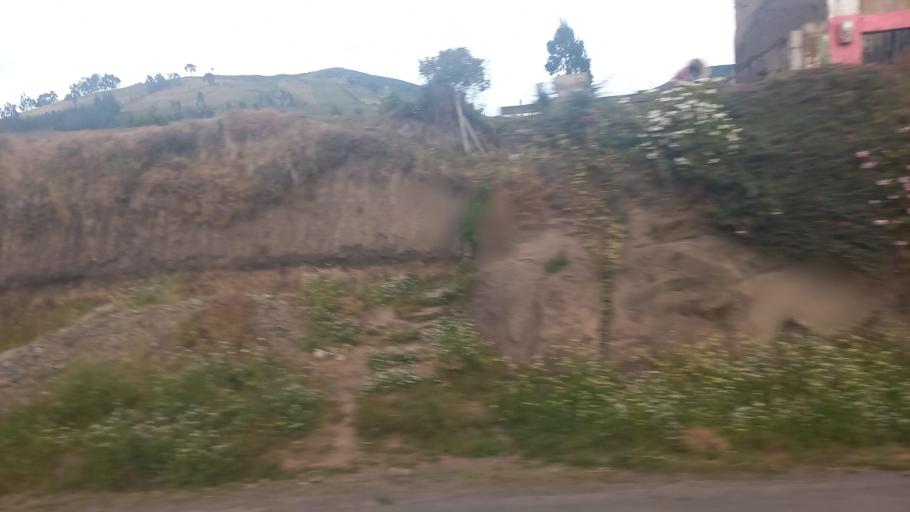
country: EC
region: Pichincha
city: Cayambe
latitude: 0.1148
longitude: -78.0779
